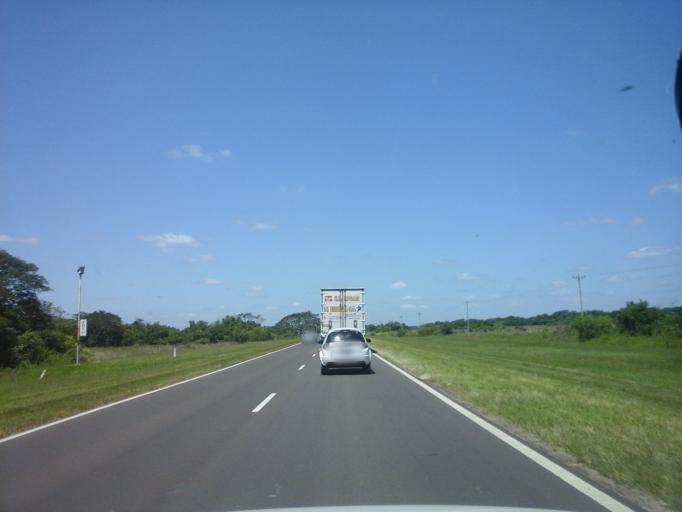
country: AR
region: Corrientes
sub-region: Departamento de Itati
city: Itati
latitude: -27.3402
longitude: -58.2129
